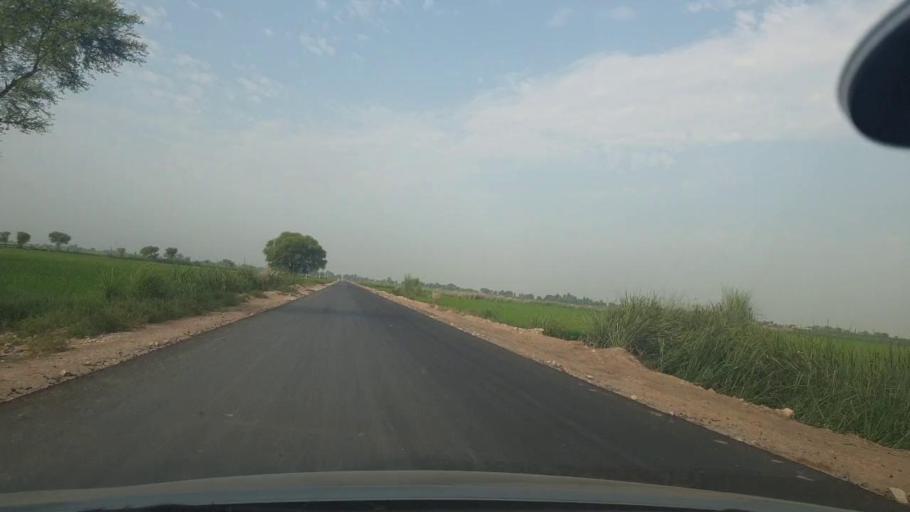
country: PK
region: Sindh
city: Jacobabad
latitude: 28.0885
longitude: 68.3215
